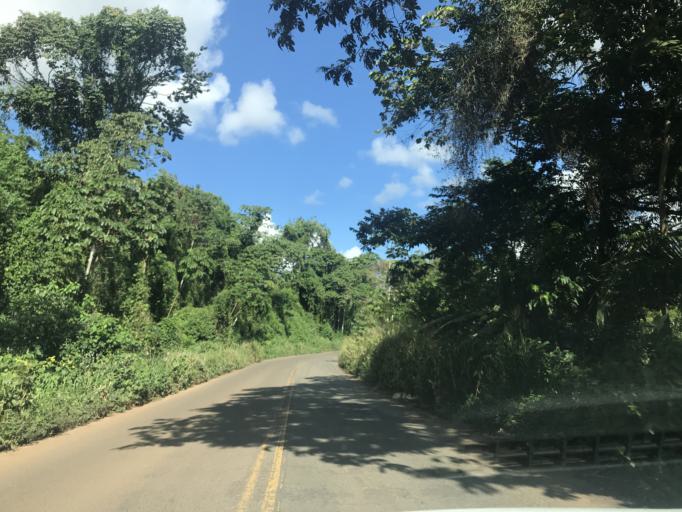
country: BR
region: Bahia
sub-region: Itubera
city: Itubera
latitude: -13.8081
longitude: -39.1492
